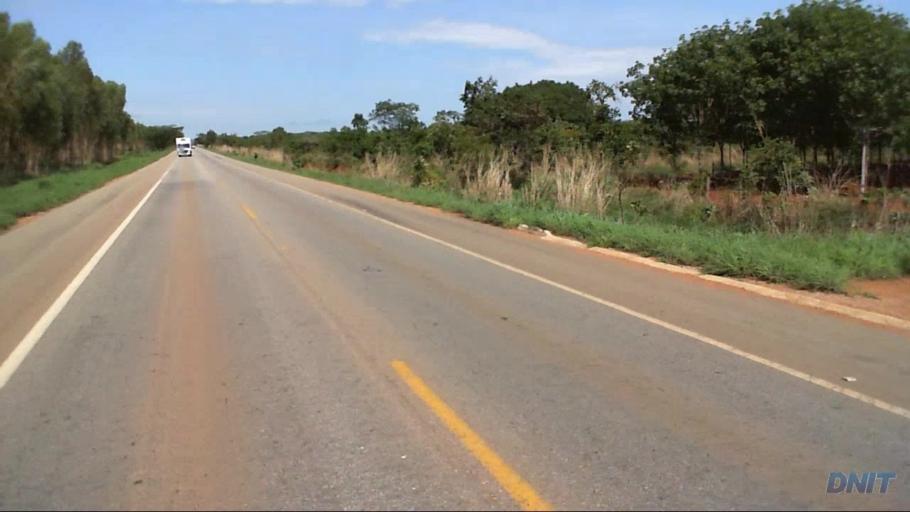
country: BR
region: Goias
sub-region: Barro Alto
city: Barro Alto
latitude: -15.2057
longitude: -48.7248
